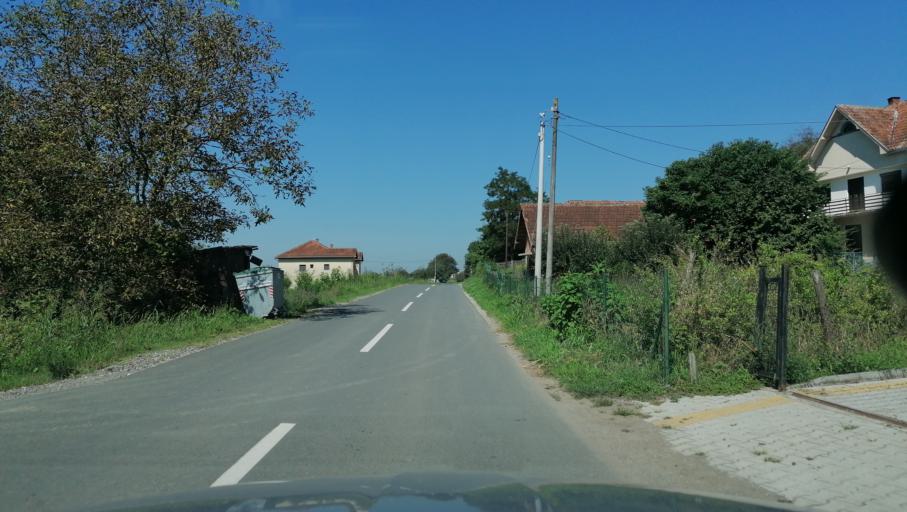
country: RS
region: Central Serbia
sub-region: Raski Okrug
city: Vrnjacka Banja
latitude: 43.6637
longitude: 20.9209
